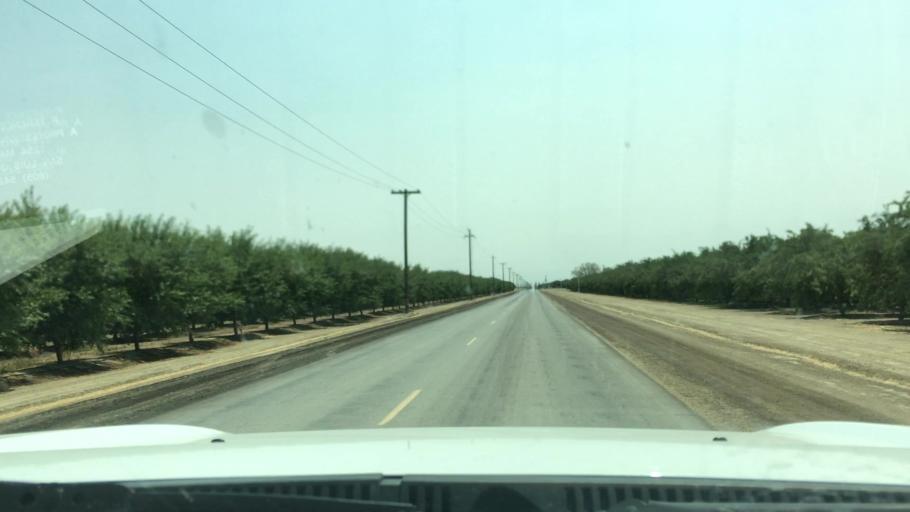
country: US
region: California
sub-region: Kern County
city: Wasco
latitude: 35.6363
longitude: -119.4377
